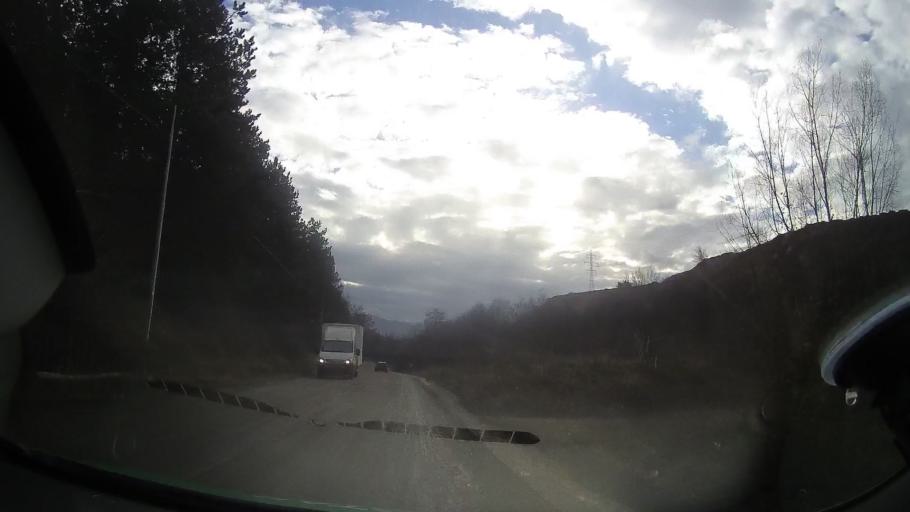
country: RO
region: Cluj
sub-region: Comuna Baisoara
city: Baisoara
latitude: 46.5860
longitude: 23.4598
